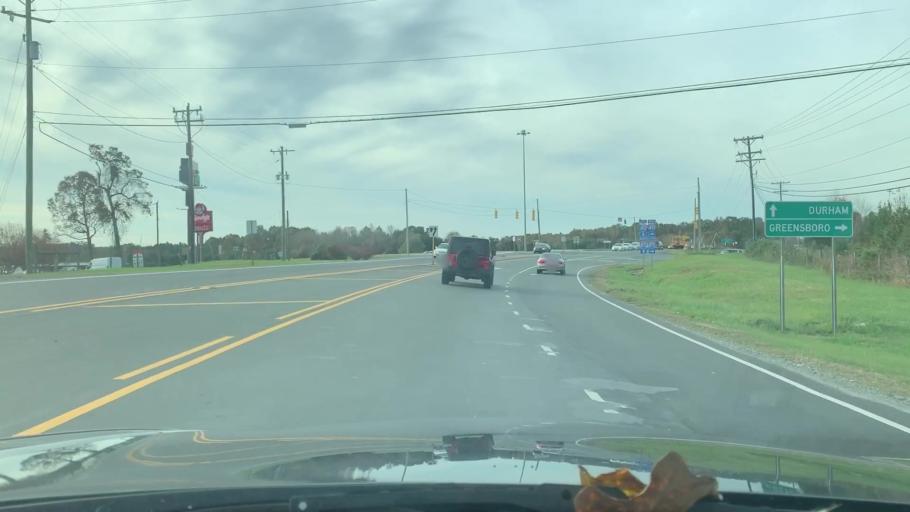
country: US
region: North Carolina
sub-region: Alamance County
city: Haw River
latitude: 36.0708
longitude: -79.3520
